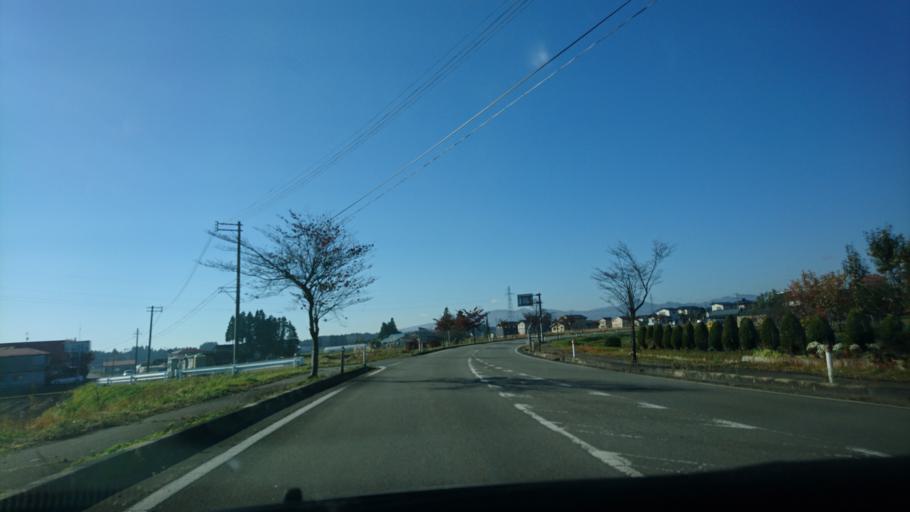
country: JP
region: Iwate
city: Mizusawa
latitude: 39.1306
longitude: 141.0644
